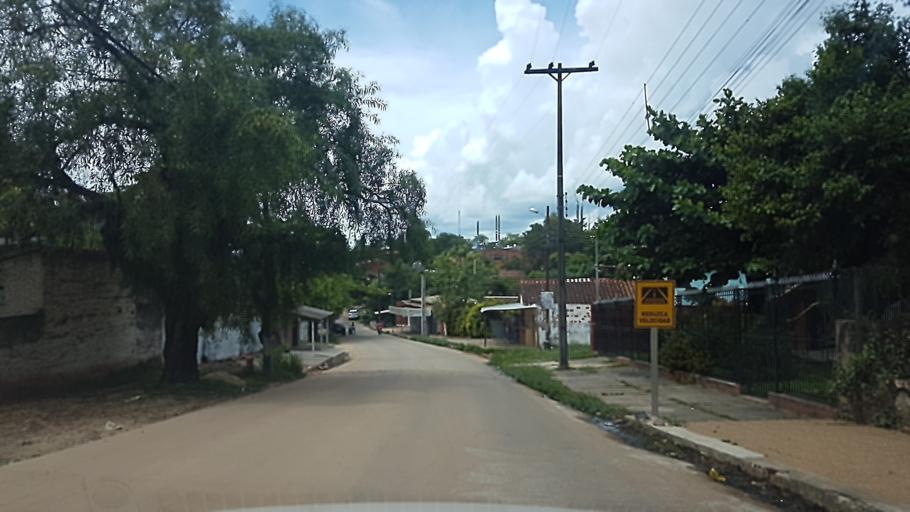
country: PY
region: Central
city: Colonia Mariano Roque Alonso
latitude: -25.1852
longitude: -57.5395
